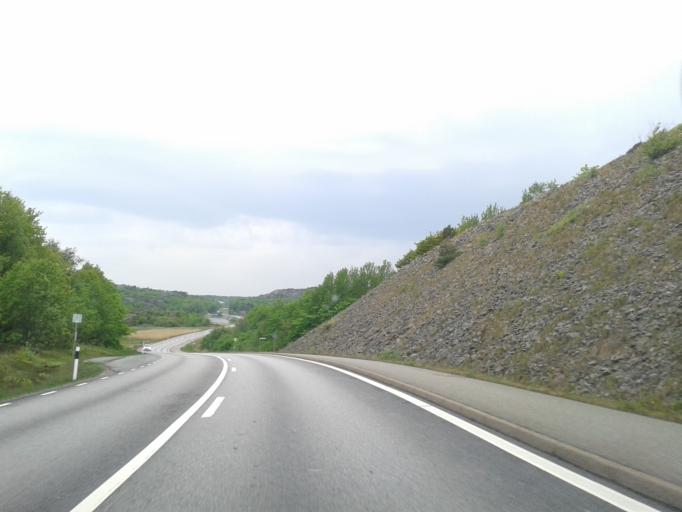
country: SE
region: Vaestra Goetaland
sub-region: Kungalvs Kommun
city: Marstrand
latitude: 57.8943
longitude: 11.6438
